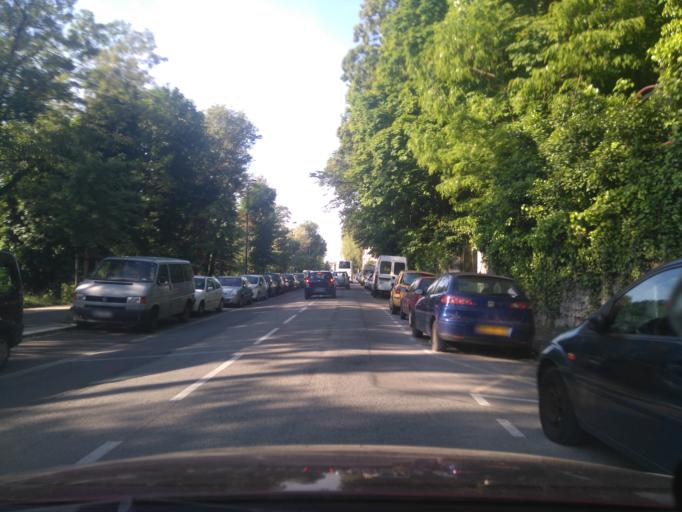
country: FR
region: Rhone-Alpes
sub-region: Departement de l'Isere
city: La Tronche
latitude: 45.2010
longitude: 5.7338
